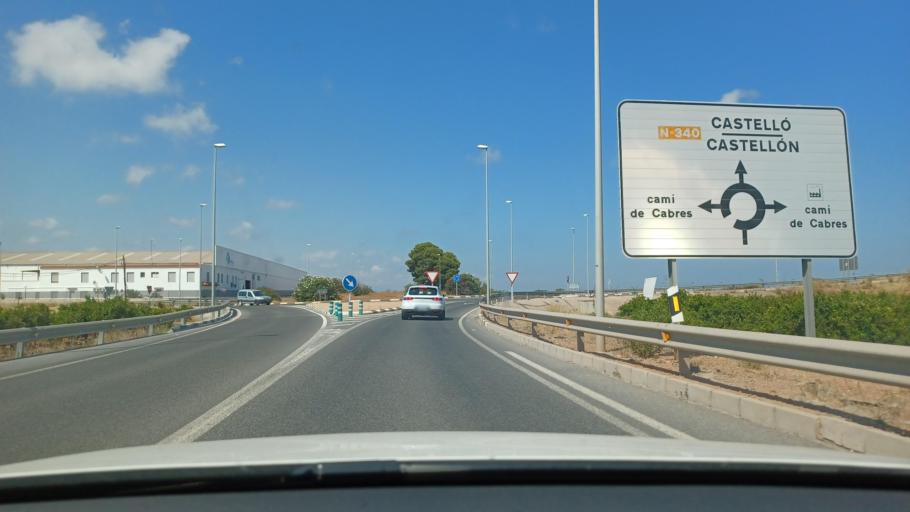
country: ES
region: Valencia
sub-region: Provincia de Castello
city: Chilches
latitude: 39.8018
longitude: -0.1759
